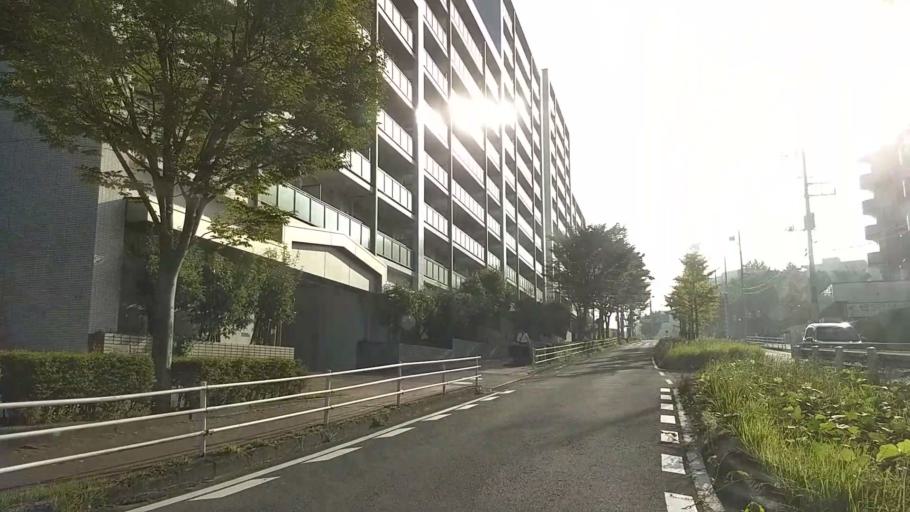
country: JP
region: Kanagawa
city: Yokohama
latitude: 35.4356
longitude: 139.5600
